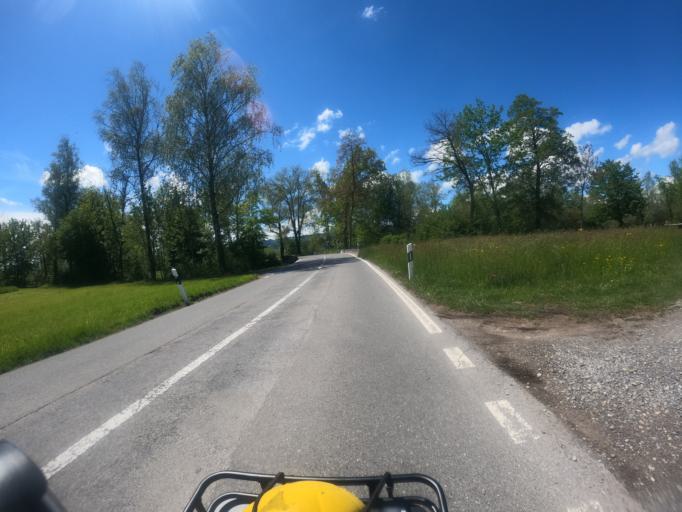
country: CH
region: Zurich
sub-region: Bezirk Affoltern
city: Obfelden / Oberlunnern
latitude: 47.2339
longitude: 8.4174
